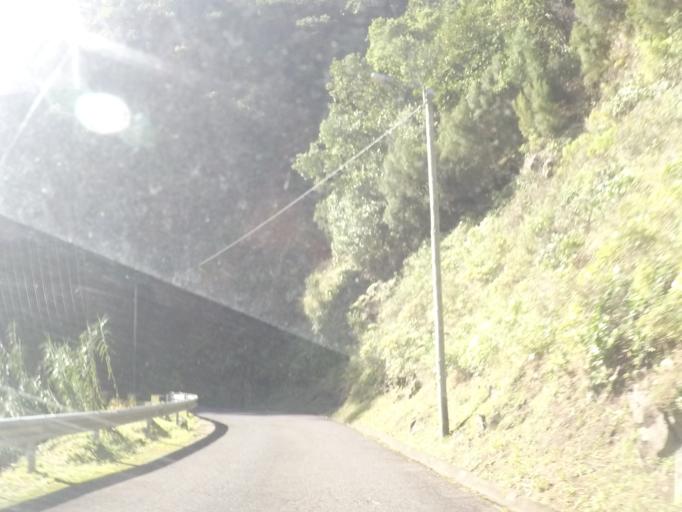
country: PT
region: Madeira
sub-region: Camara de Lobos
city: Curral das Freiras
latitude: 32.7864
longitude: -16.9742
